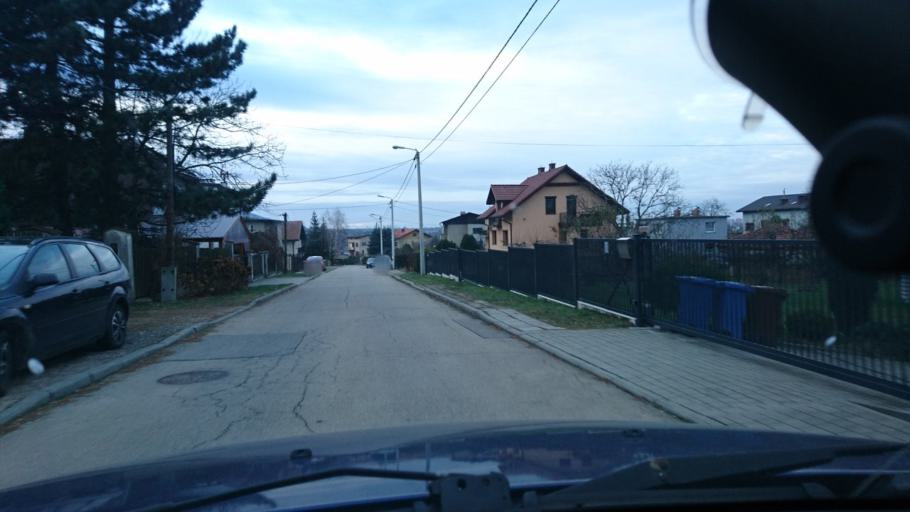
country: PL
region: Silesian Voivodeship
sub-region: Bielsko-Biala
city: Bielsko-Biala
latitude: 49.7980
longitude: 19.0666
